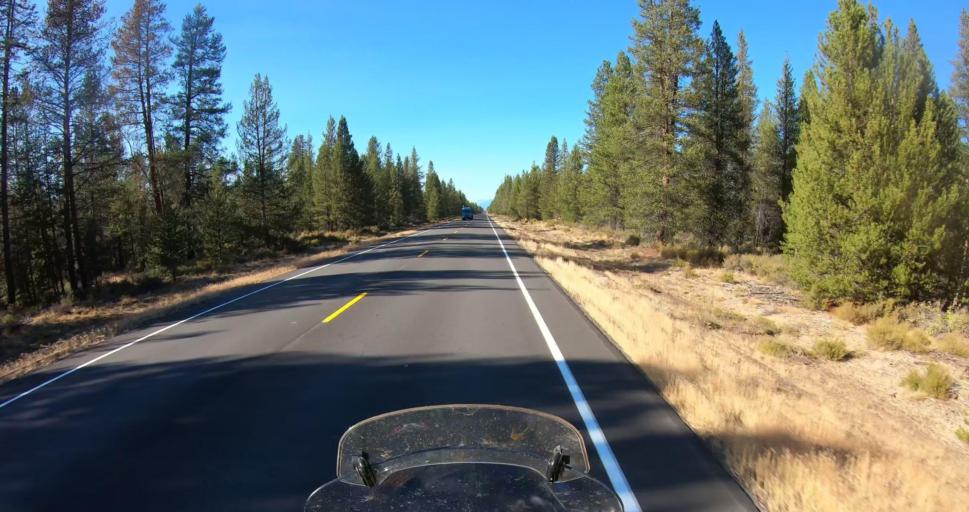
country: US
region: Oregon
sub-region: Deschutes County
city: La Pine
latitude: 43.5262
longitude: -121.4585
